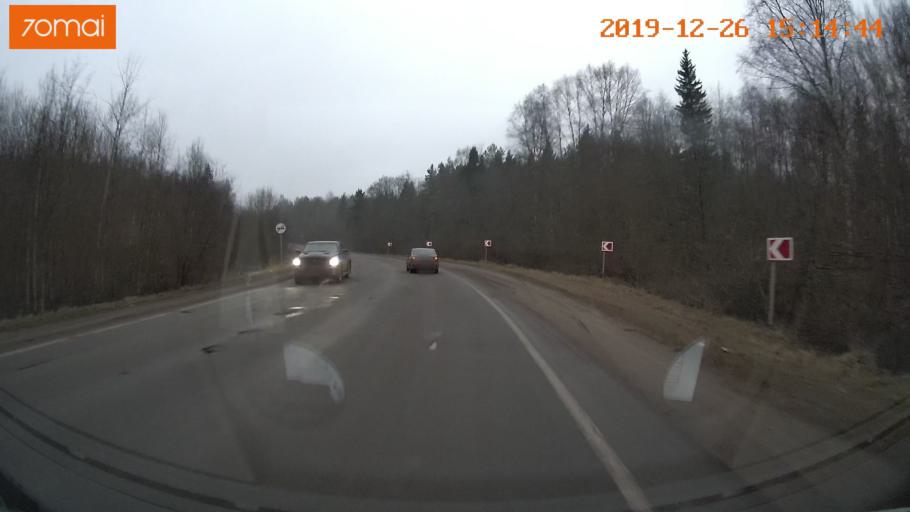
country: RU
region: Jaroslavl
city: Rybinsk
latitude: 58.1035
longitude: 38.8774
